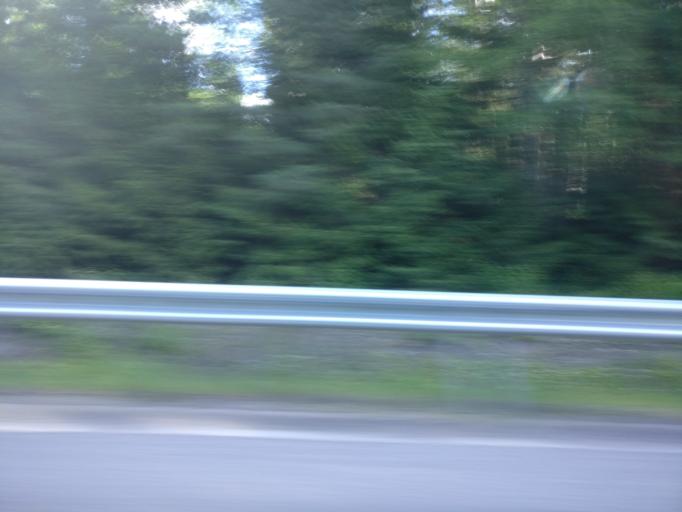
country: FI
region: Uusimaa
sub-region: Helsinki
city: Vihti
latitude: 60.4337
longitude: 24.4759
